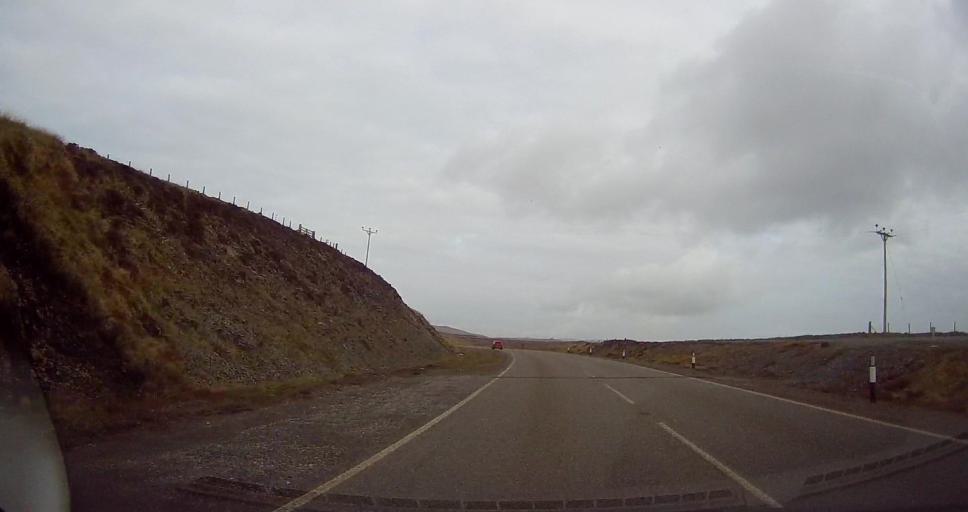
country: GB
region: Scotland
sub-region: Shetland Islands
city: Sandwick
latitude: 60.0766
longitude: -1.2295
